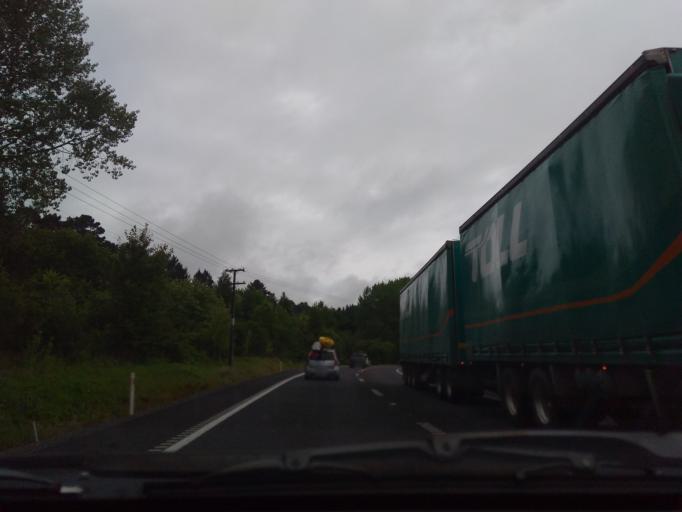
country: NZ
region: Auckland
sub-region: Auckland
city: Wellsford
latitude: -36.1267
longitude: 174.4310
